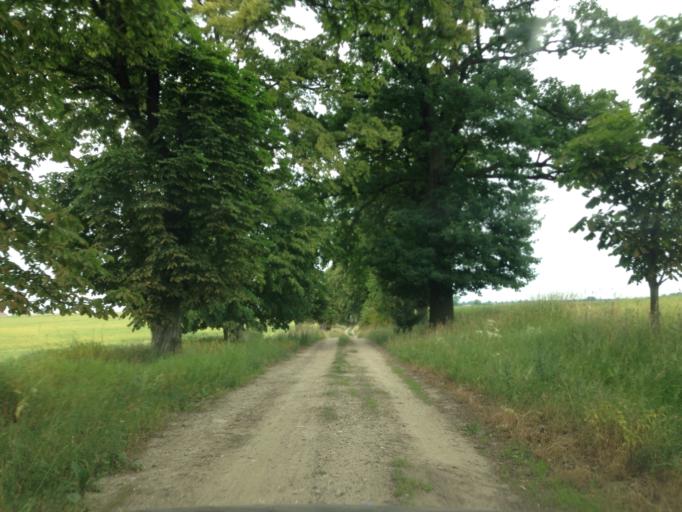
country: PL
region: Kujawsko-Pomorskie
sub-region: Powiat brodnicki
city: Bobrowo
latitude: 53.2132
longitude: 19.2427
